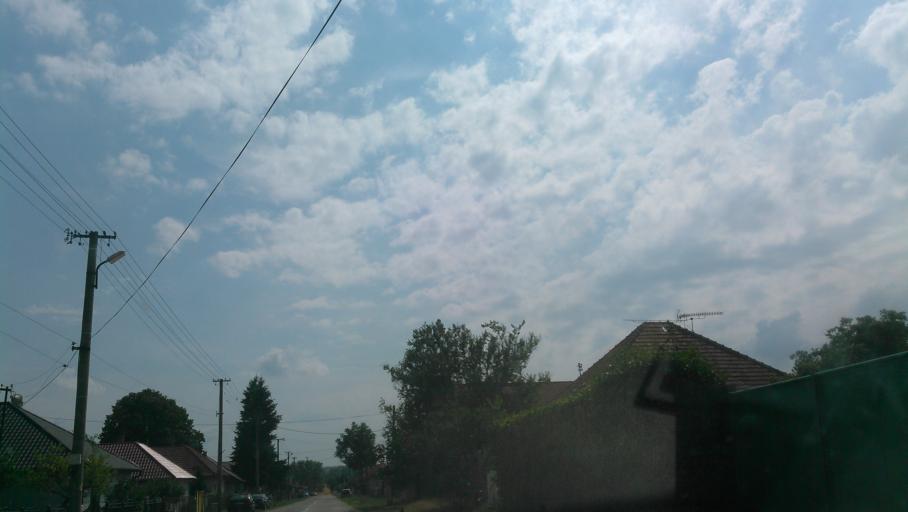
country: SK
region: Nitriansky
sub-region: Okres Nitra
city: Nitra
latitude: 48.4844
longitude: 18.0347
